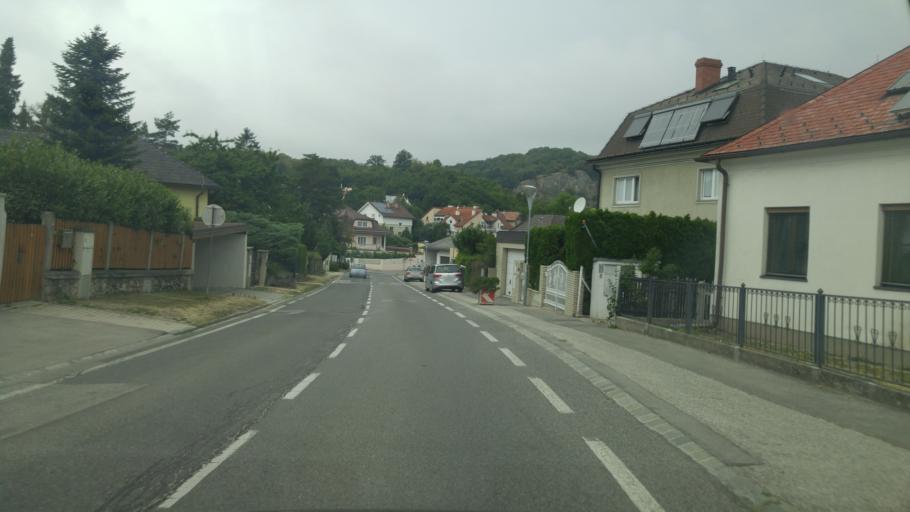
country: AT
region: Lower Austria
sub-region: Politischer Bezirk Modling
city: Giesshubl
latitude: 48.0991
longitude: 16.2394
